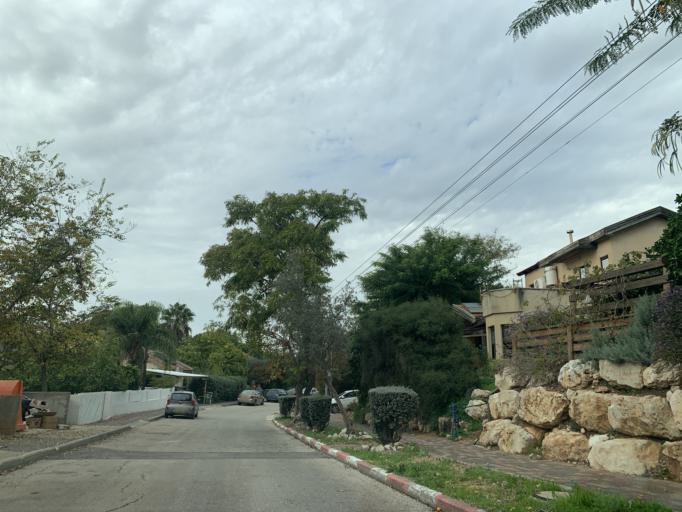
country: IL
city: Nirit
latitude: 32.1450
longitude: 34.9840
